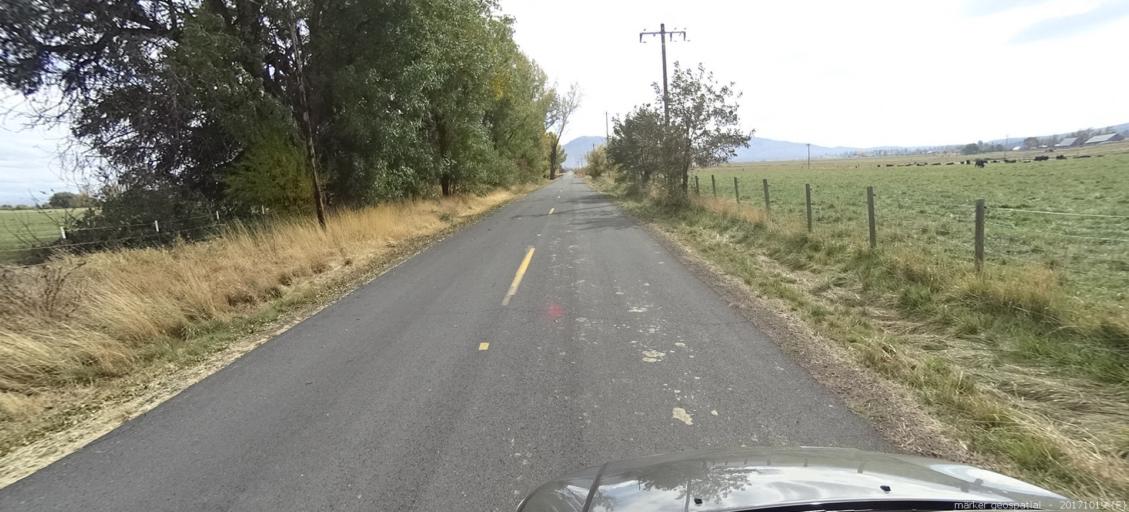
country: US
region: California
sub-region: Shasta County
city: Burney
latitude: 41.0961
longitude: -121.4932
